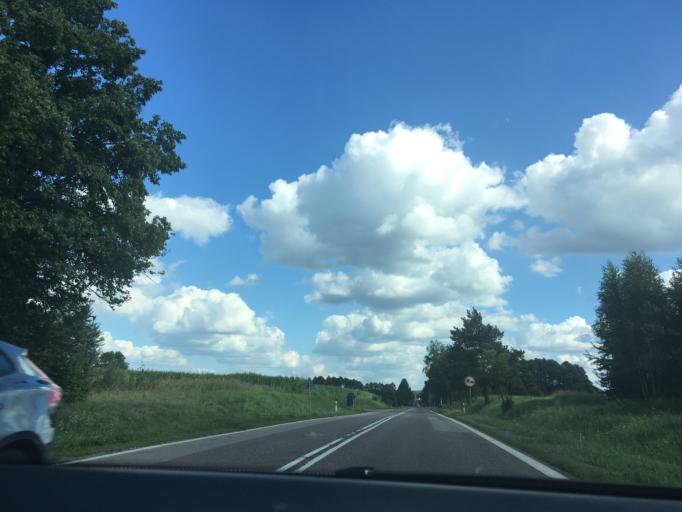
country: PL
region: Podlasie
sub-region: Powiat bialostocki
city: Dobrzyniewo Duze
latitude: 53.3369
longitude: 23.1053
